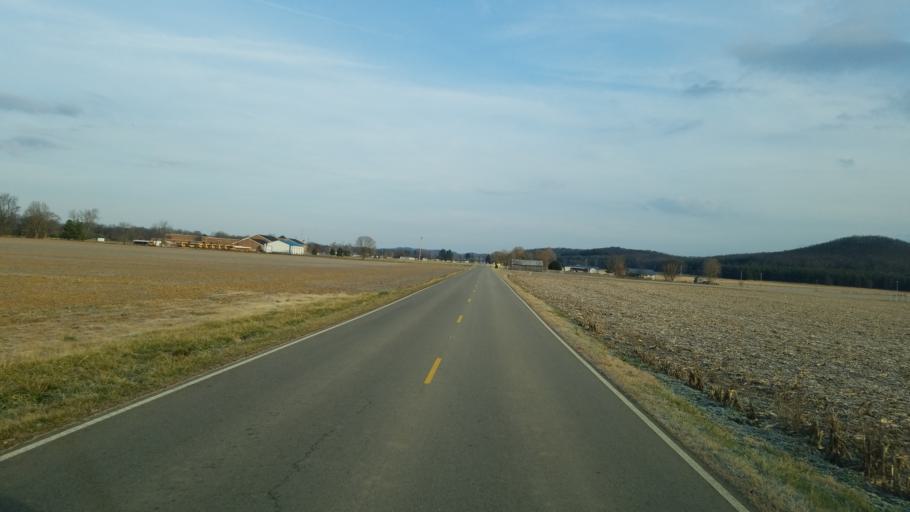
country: US
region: Ohio
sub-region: Ross County
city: Chillicothe
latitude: 39.2751
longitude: -82.8691
